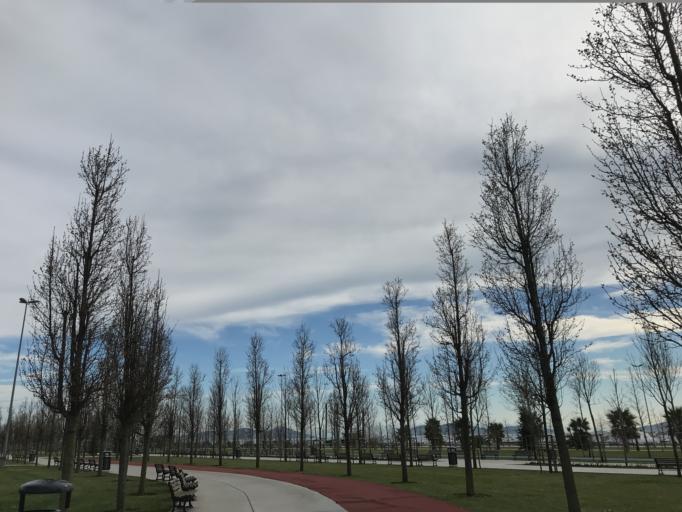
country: TR
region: Istanbul
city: Maltepe
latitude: 40.9372
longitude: 29.1099
